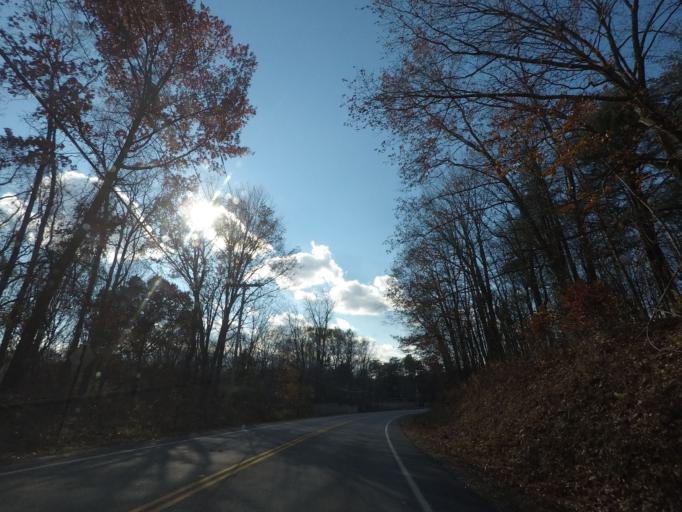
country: US
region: New York
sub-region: Saratoga County
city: Country Knolls
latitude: 42.8868
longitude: -73.7934
